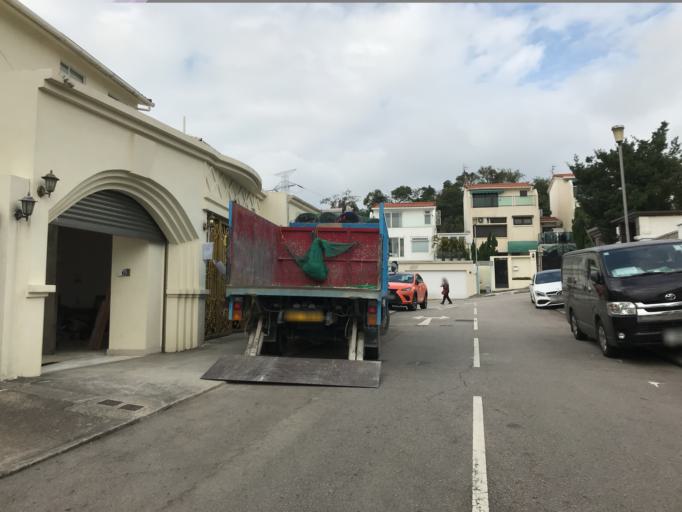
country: HK
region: Tai Po
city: Tai Po
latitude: 22.4650
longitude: 114.1572
